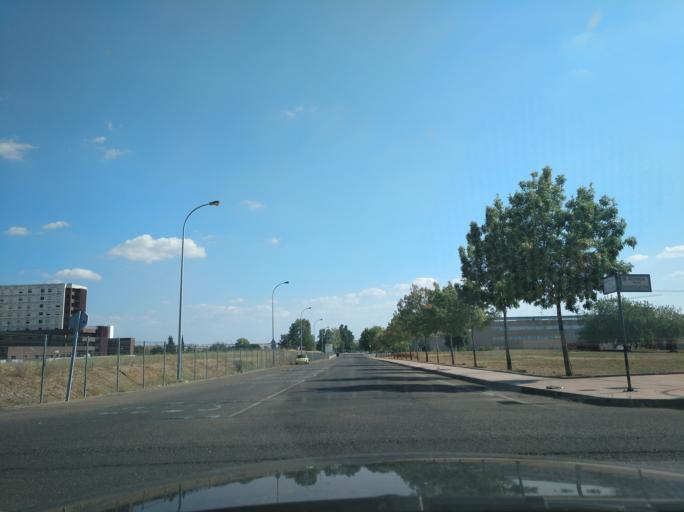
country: ES
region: Extremadura
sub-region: Provincia de Badajoz
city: Badajoz
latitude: 38.8862
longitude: -7.0034
